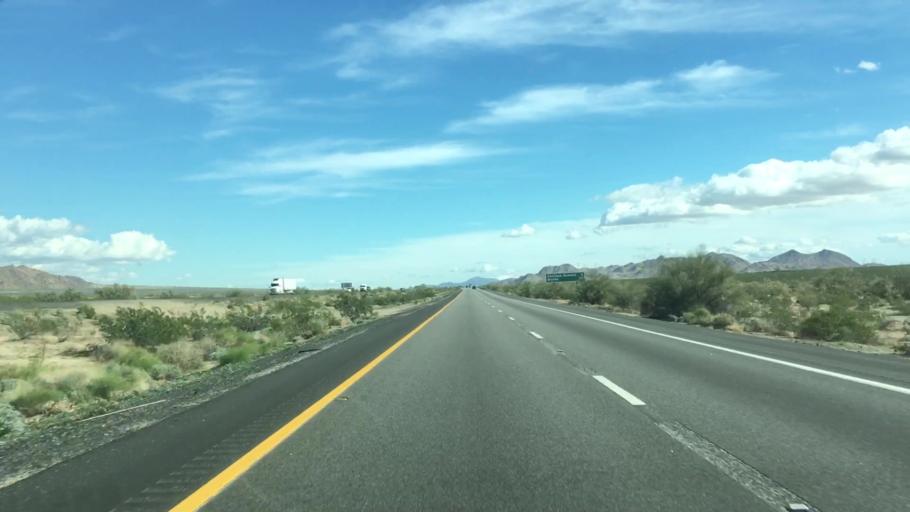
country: US
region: California
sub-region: Riverside County
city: Mecca
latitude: 33.6600
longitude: -115.7902
